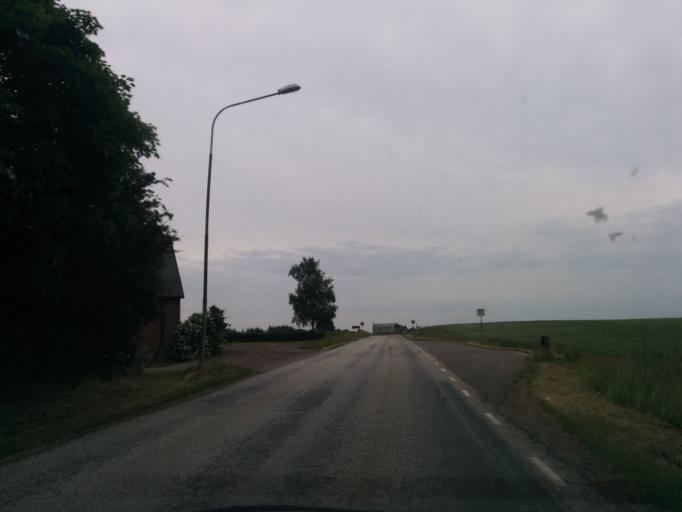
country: SE
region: Skane
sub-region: Lunds Kommun
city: Genarp
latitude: 55.6448
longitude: 13.3489
